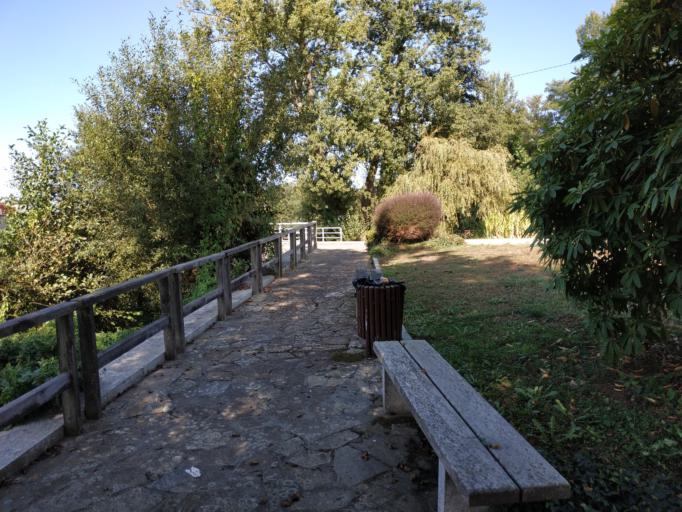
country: ES
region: Galicia
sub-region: Provincia da Coruna
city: Laracha
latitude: 43.2501
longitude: -8.6118
